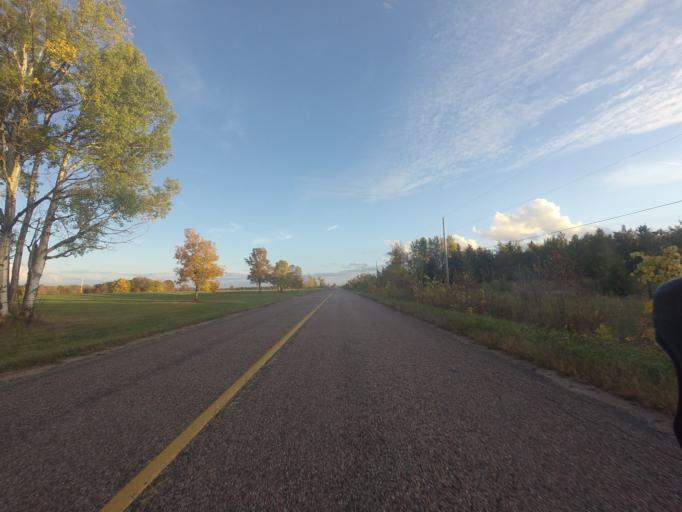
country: CA
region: Ontario
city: Renfrew
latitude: 45.4610
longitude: -76.9757
